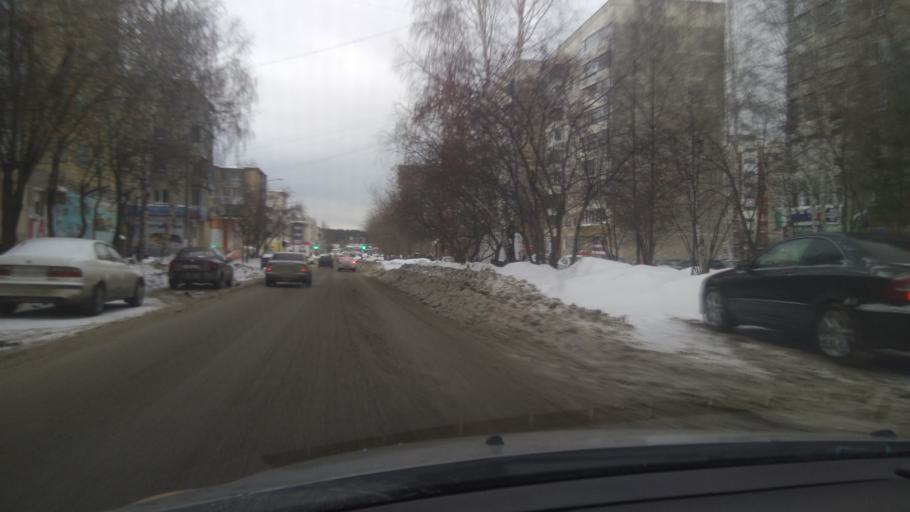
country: RU
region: Sverdlovsk
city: Verkhnyaya Pyshma
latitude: 56.9796
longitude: 60.5593
